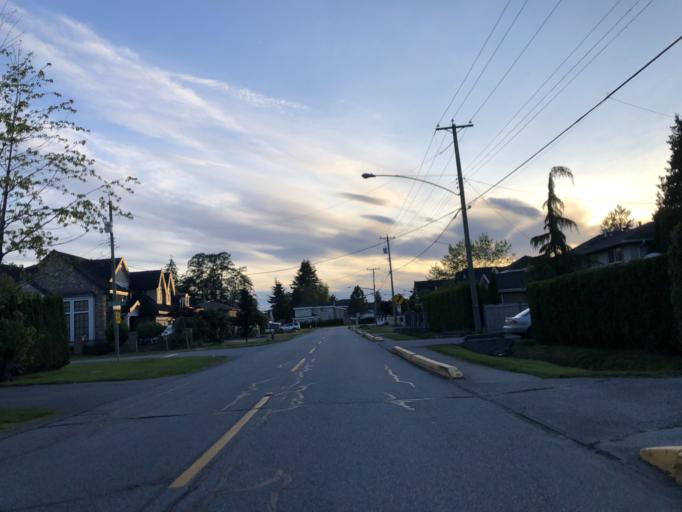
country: CA
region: British Columbia
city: Richmond
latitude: 49.1432
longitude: -123.1219
